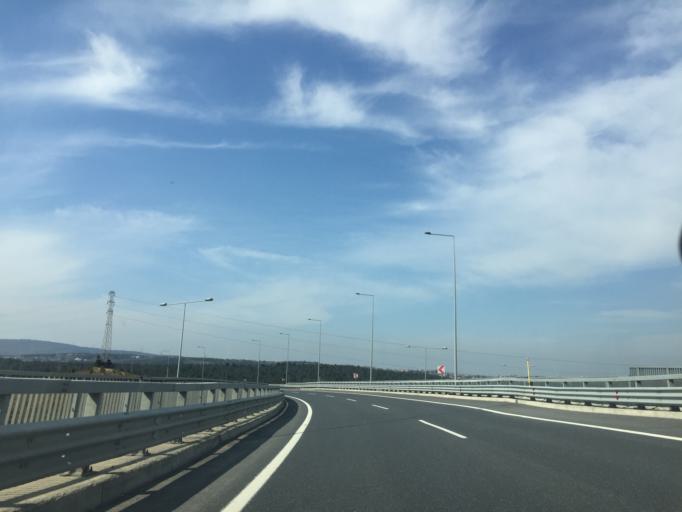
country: TR
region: Istanbul
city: Sancaktepe
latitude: 41.0494
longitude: 29.2774
